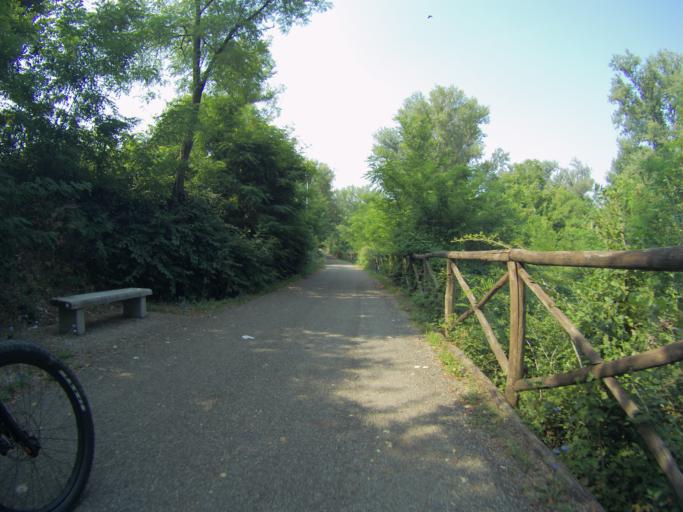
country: IT
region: Emilia-Romagna
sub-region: Provincia di Reggio Emilia
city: Pratissolo
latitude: 44.5935
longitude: 10.6759
